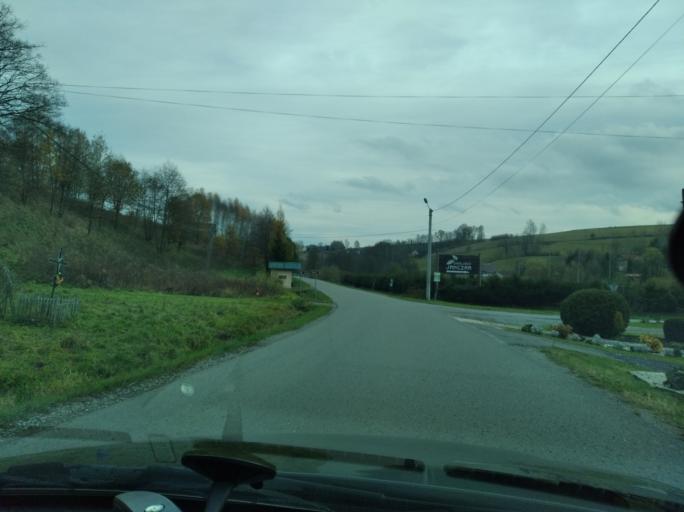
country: PL
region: Subcarpathian Voivodeship
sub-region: Powiat ropczycko-sedziszowski
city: Iwierzyce
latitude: 49.9483
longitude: 21.7308
